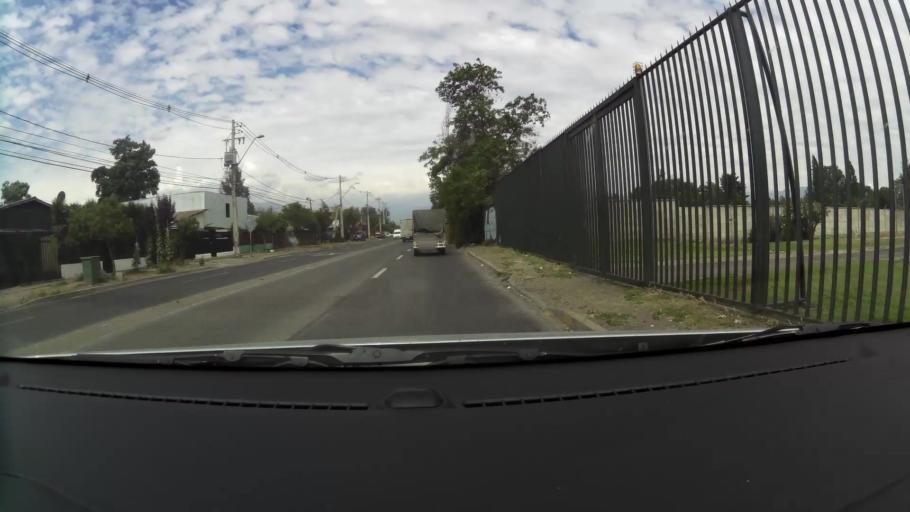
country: CL
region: Santiago Metropolitan
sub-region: Provincia de Santiago
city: La Pintana
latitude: -33.5860
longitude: -70.6581
